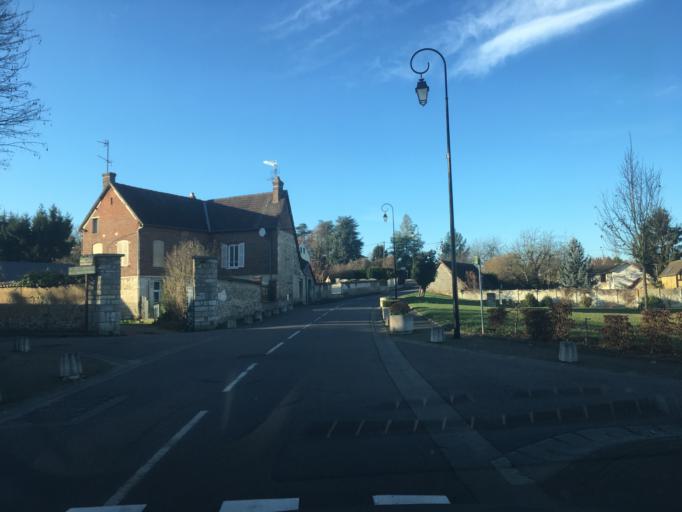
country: FR
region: Haute-Normandie
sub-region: Departement de l'Eure
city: Saint-Marcel
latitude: 49.0955
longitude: 1.4495
